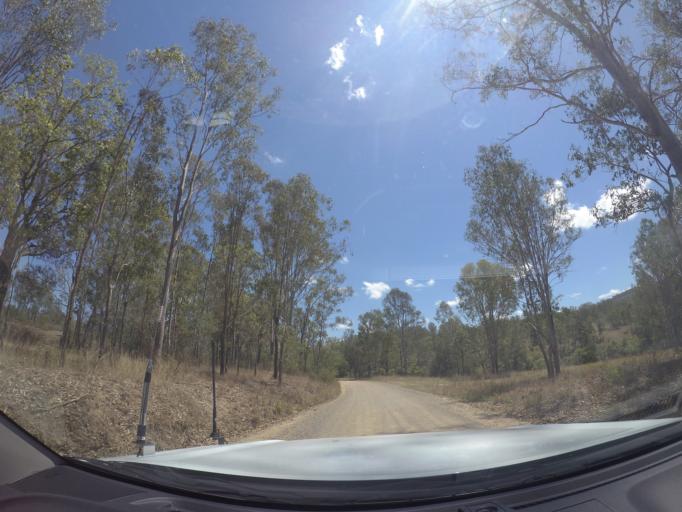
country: AU
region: Queensland
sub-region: Logan
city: North Maclean
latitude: -27.8289
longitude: 152.8644
